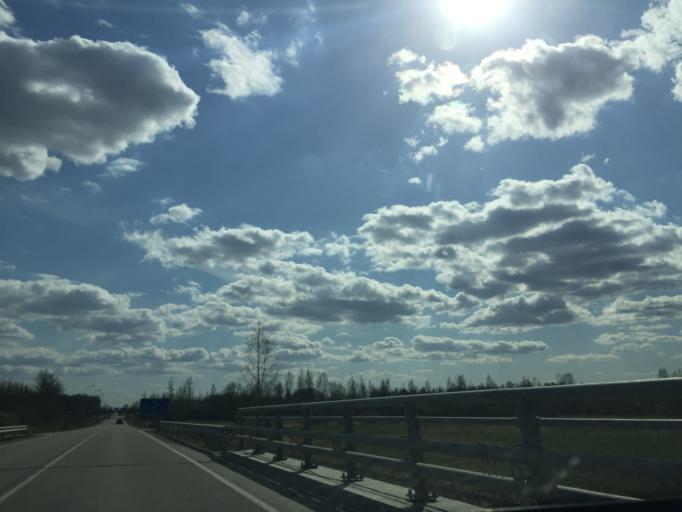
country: LV
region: Skriveri
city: Skriveri
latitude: 56.7356
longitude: 25.1635
